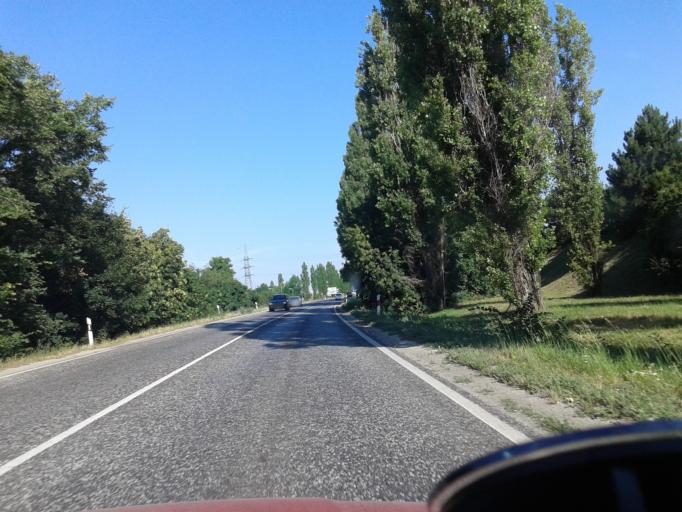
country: HU
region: Pest
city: Biatorbagy
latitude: 47.4736
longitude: 18.8474
